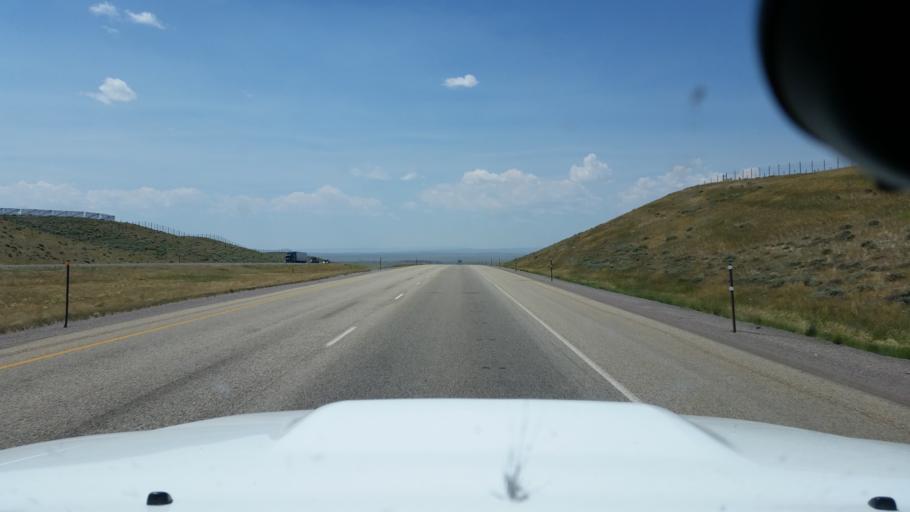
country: US
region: Wyoming
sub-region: Carbon County
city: Saratoga
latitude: 41.7340
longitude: -106.6466
